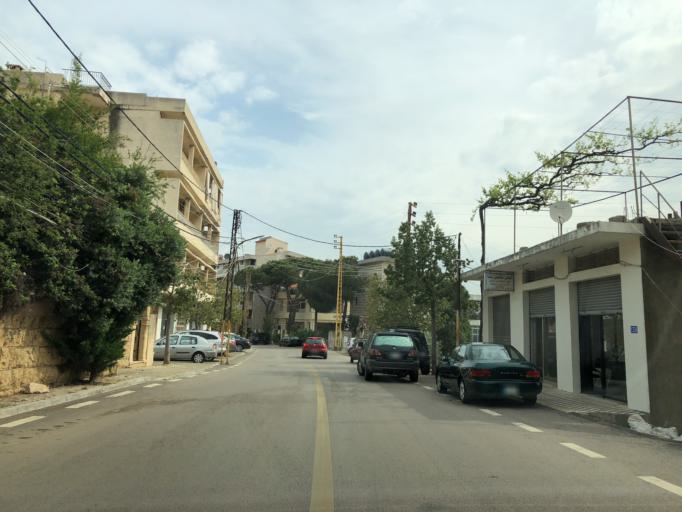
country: LB
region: Mont-Liban
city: Jdaidet el Matn
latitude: 33.8671
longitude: 35.6079
